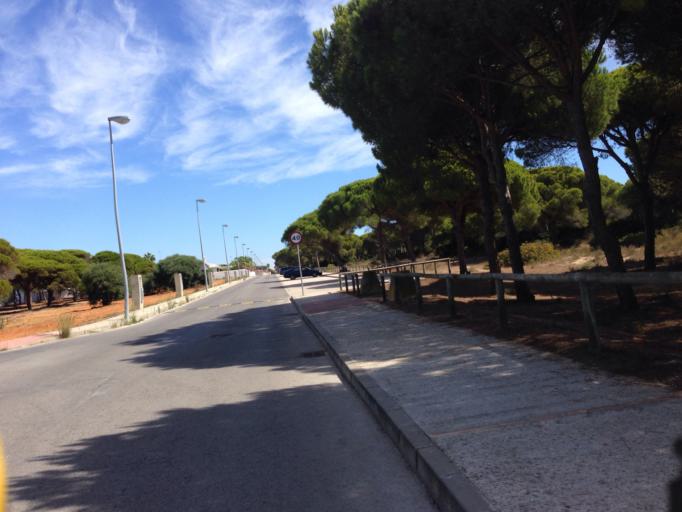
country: ES
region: Andalusia
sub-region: Provincia de Cadiz
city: Chiclana de la Frontera
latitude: 36.3784
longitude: -6.1970
